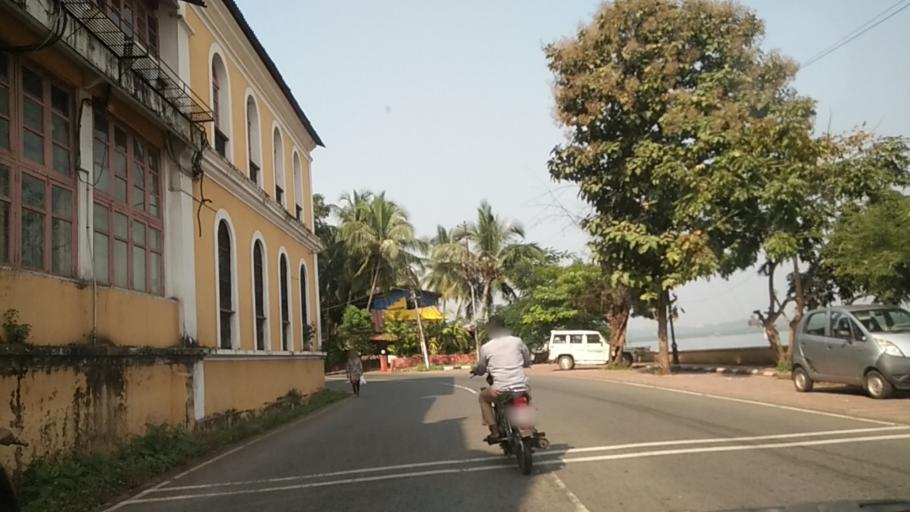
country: IN
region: Goa
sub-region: North Goa
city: Bambolim
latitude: 15.5021
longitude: 73.8743
